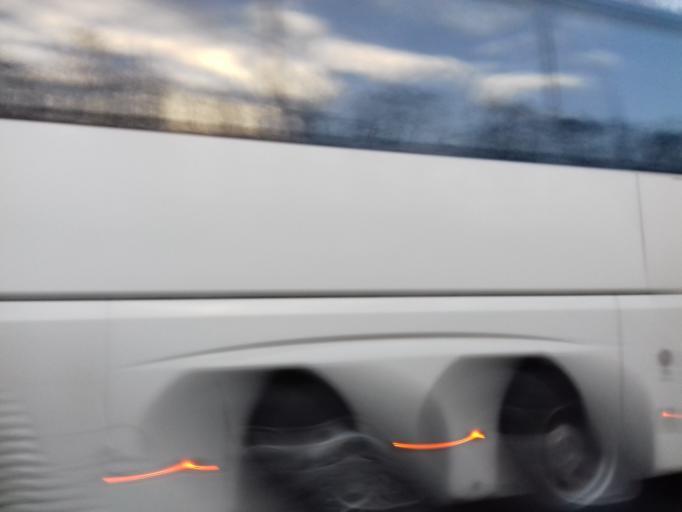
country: IE
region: Ulster
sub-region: County Monaghan
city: Castleblayney
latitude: 54.0907
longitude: -6.7167
